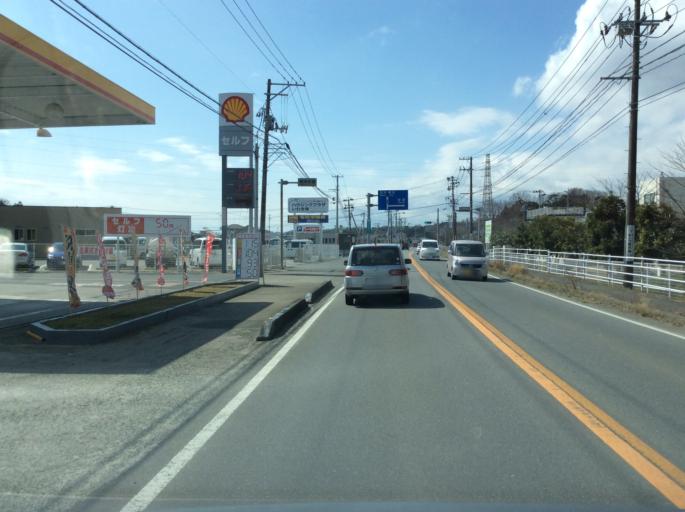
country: JP
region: Fukushima
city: Iwaki
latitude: 36.9461
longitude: 140.8582
